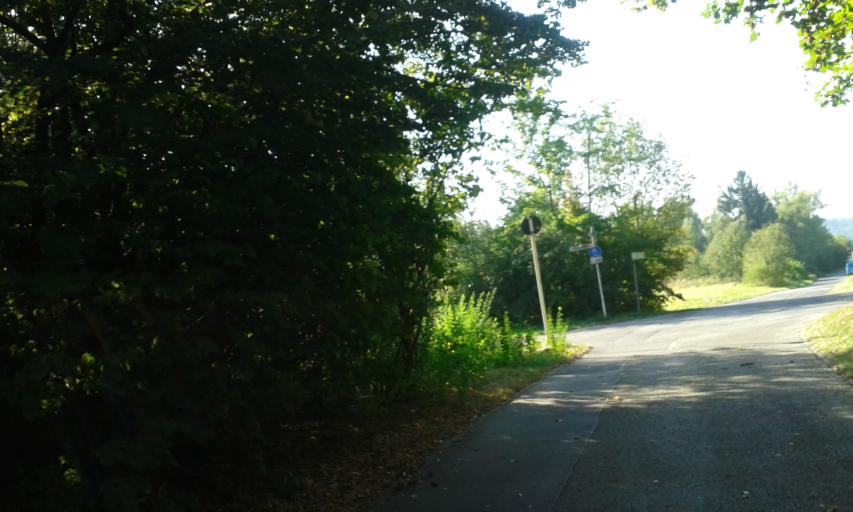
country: DE
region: Bavaria
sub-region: Upper Franconia
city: Bamberg
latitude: 49.8719
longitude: 10.8833
